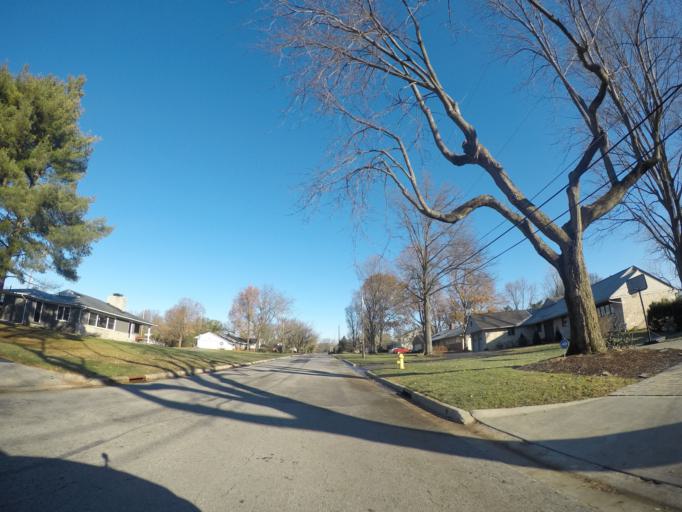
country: US
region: Ohio
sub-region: Franklin County
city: Upper Arlington
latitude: 40.0377
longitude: -83.0631
